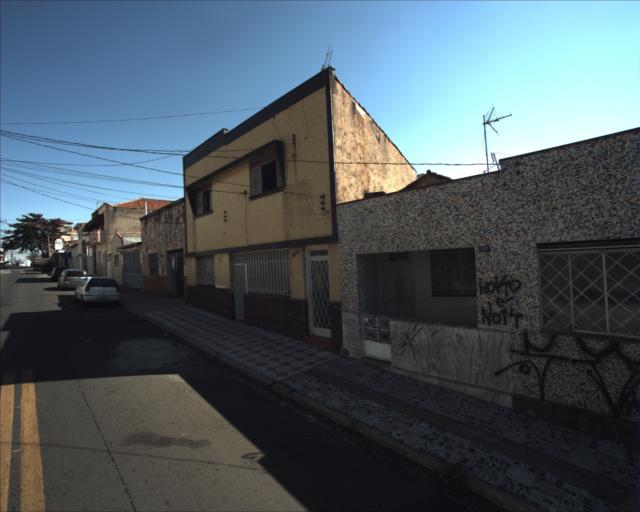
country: BR
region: Sao Paulo
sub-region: Sorocaba
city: Sorocaba
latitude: -23.5043
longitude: -47.4441
